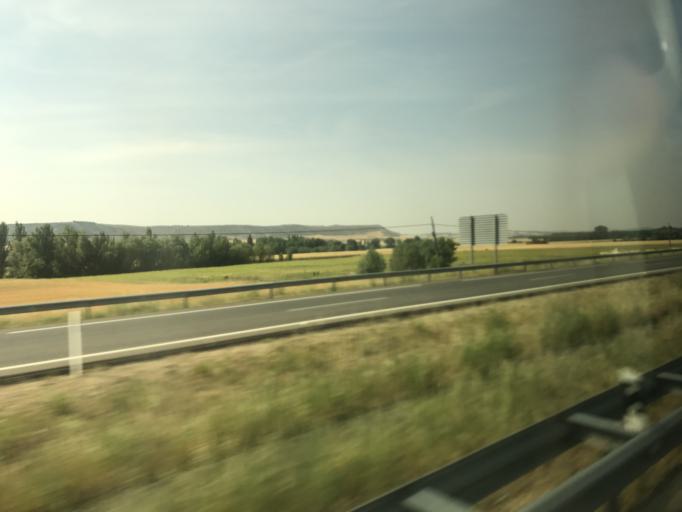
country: ES
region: Castille and Leon
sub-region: Provincia de Palencia
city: Villodrigo
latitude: 42.1325
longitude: -4.1227
